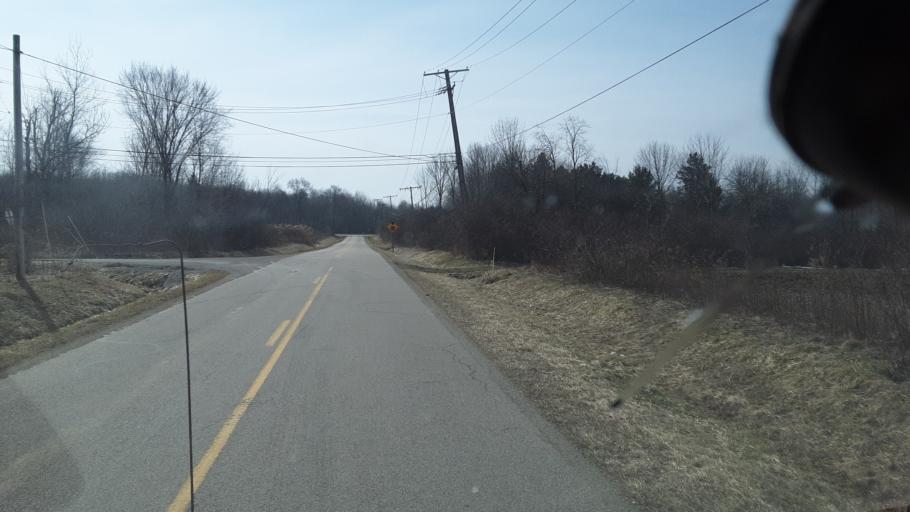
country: US
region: Ohio
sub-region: Ashtabula County
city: Jefferson
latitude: 41.7494
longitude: -80.7415
